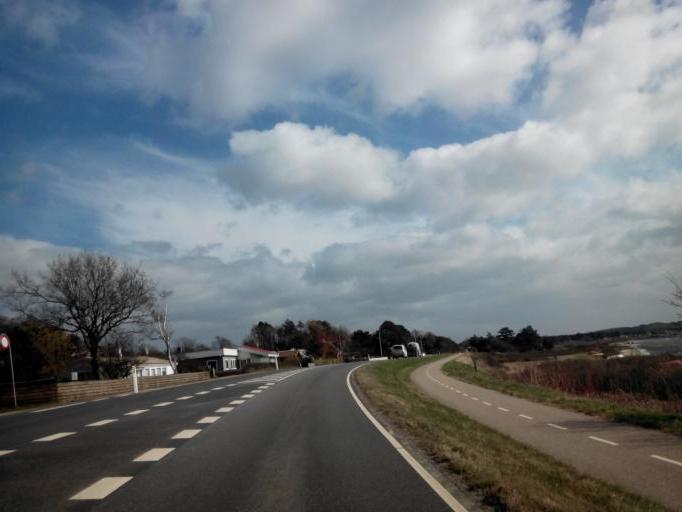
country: DK
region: Central Jutland
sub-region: Syddjurs Kommune
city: Ebeltoft
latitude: 56.2257
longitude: 10.6549
